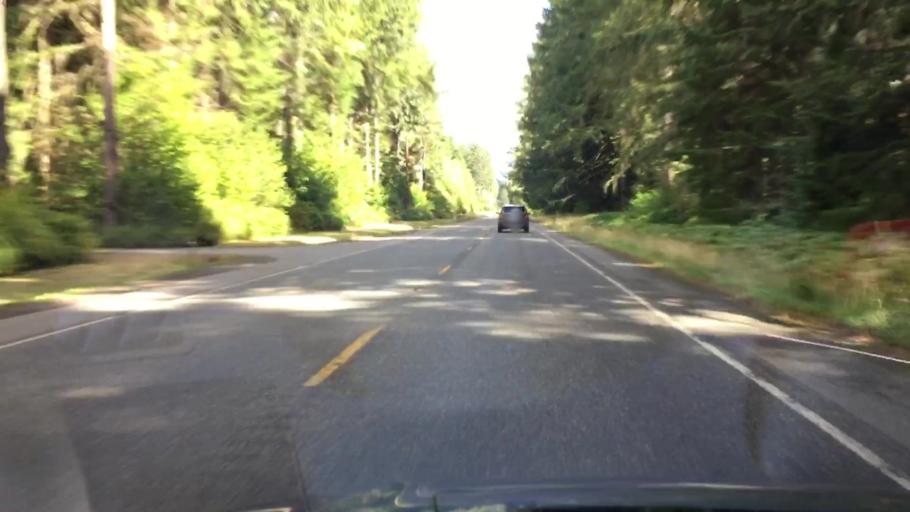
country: US
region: Washington
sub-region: Pierce County
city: Eatonville
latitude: 46.7563
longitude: -122.0755
